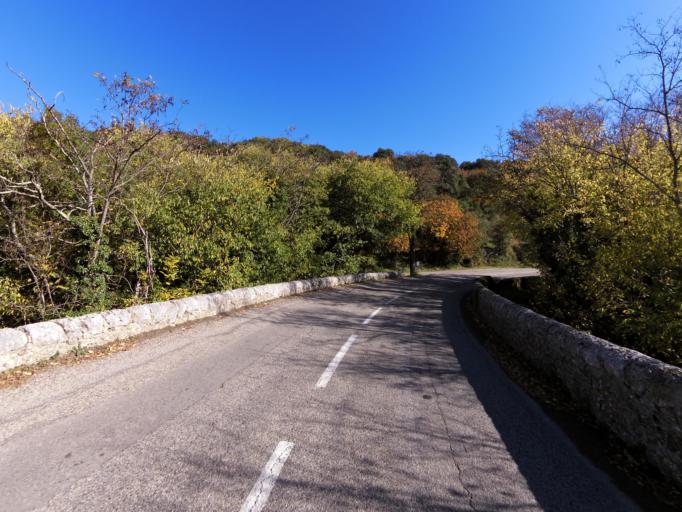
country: FR
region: Rhone-Alpes
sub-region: Departement de l'Ardeche
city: Ruoms
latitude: 44.4043
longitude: 4.4150
